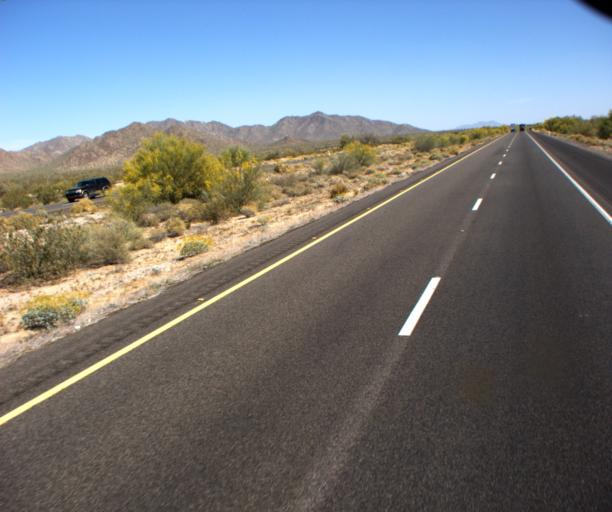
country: US
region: Arizona
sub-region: Maricopa County
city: Gila Bend
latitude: 32.8793
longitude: -112.4545
